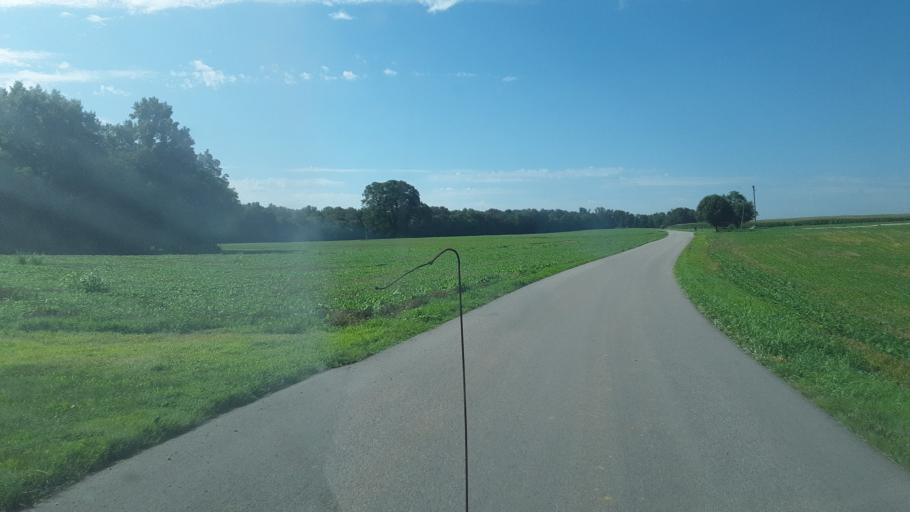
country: US
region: Kentucky
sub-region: Todd County
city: Guthrie
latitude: 36.7084
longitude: -87.1703
